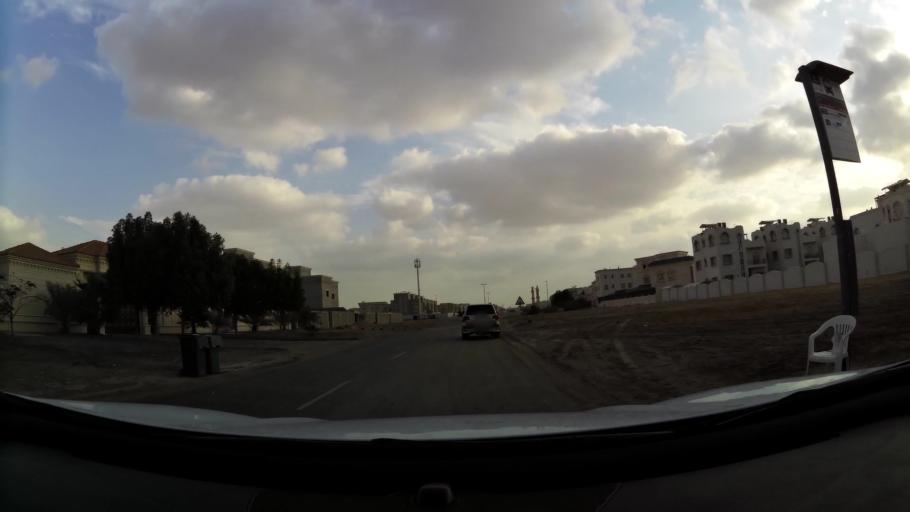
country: AE
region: Abu Dhabi
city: Abu Dhabi
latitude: 24.3580
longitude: 54.5586
